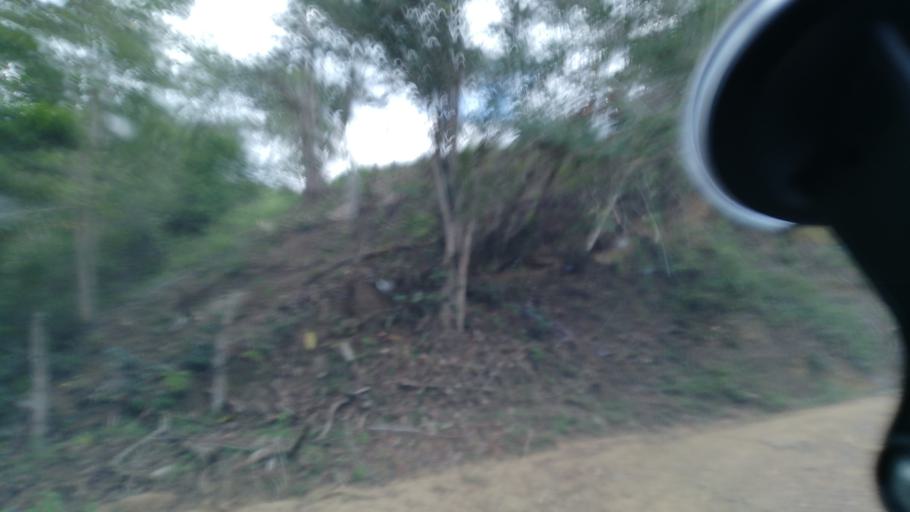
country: CO
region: Cundinamarca
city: Viani
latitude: 4.8127
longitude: -74.6152
